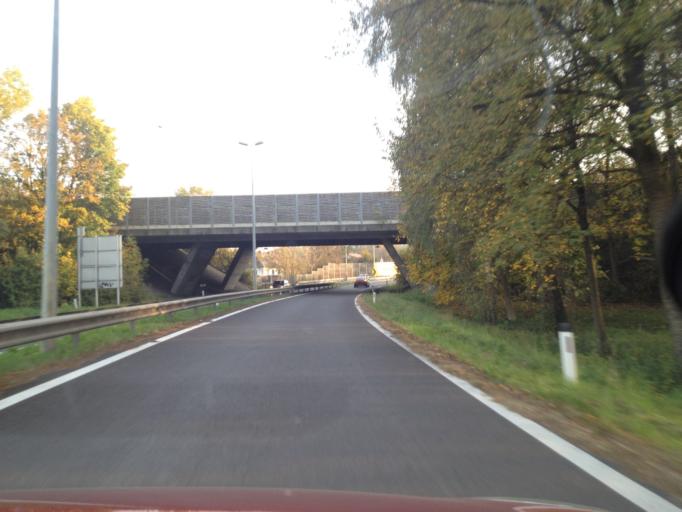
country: AT
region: Upper Austria
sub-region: Linz Stadt
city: Linz
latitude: 48.3278
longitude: 14.3187
